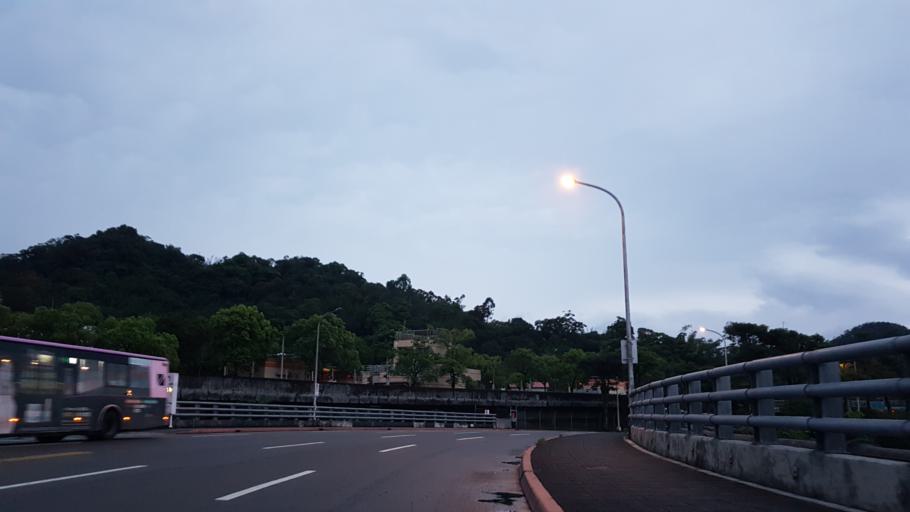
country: TW
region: Taipei
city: Taipei
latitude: 25.0017
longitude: 121.5842
